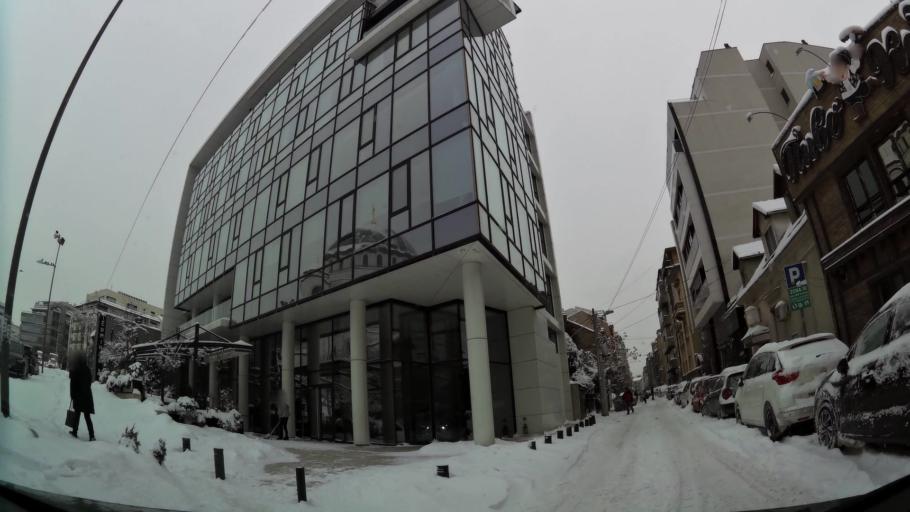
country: RS
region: Central Serbia
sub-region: Belgrade
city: Vracar
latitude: 44.7967
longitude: 20.4694
